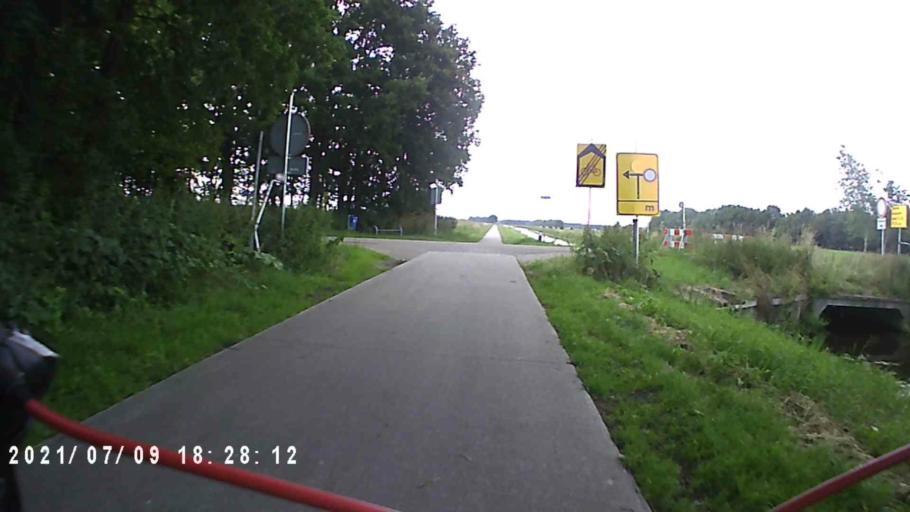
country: NL
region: Groningen
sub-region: Gemeente Pekela
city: Oude Pekela
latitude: 53.0586
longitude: 6.9820
